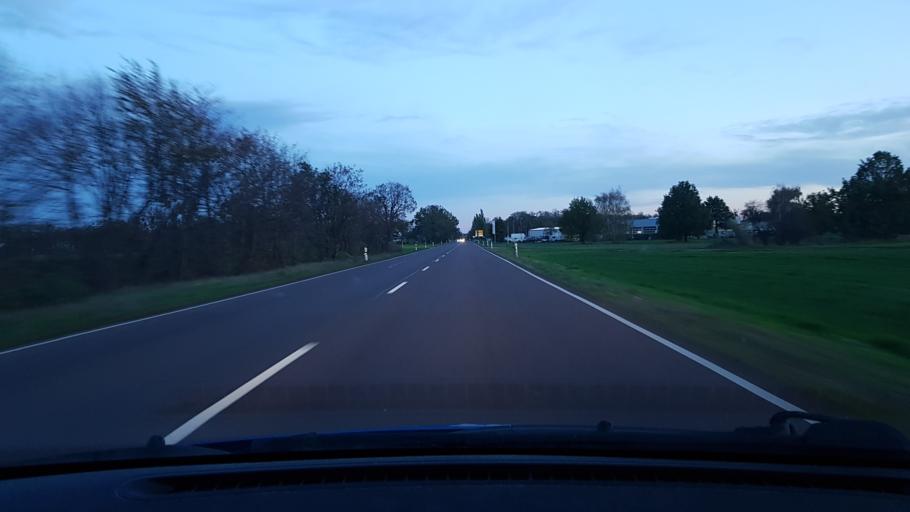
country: DE
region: Saxony-Anhalt
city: Zerbst
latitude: 51.9808
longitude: 12.0576
